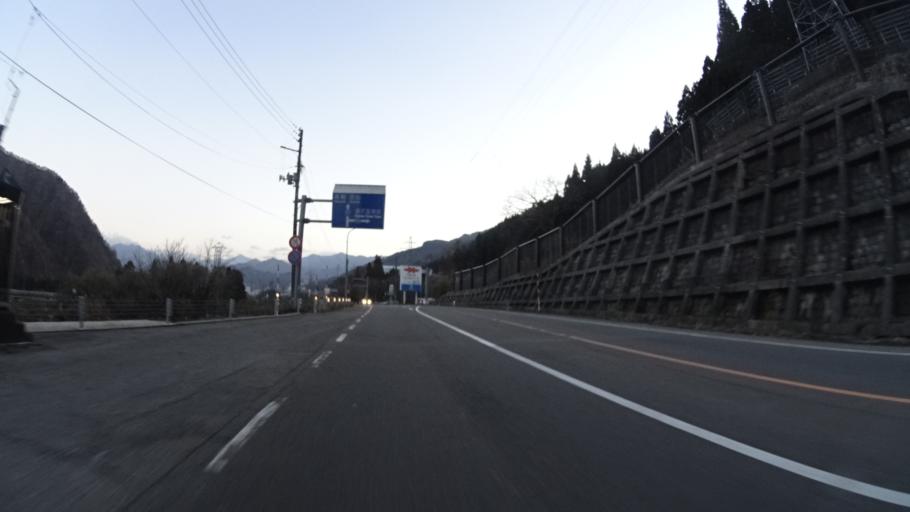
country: JP
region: Niigata
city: Shiozawa
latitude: 36.9559
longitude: 138.7990
